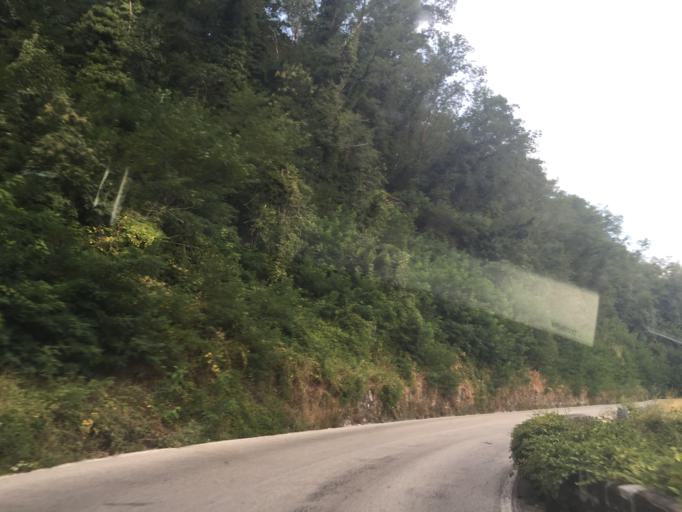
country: IT
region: Tuscany
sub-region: Provincia di Pistoia
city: Campo Tizzoro
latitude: 43.9829
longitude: 10.8621
